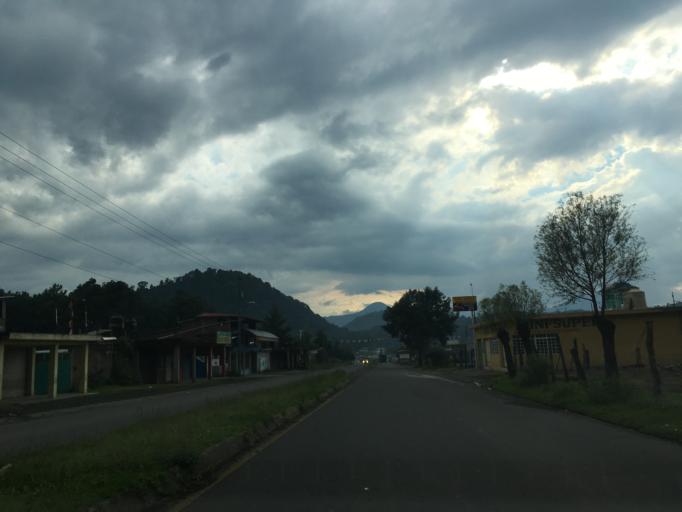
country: MX
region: Michoacan
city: Capacuaro
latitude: 19.5262
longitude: -102.1029
